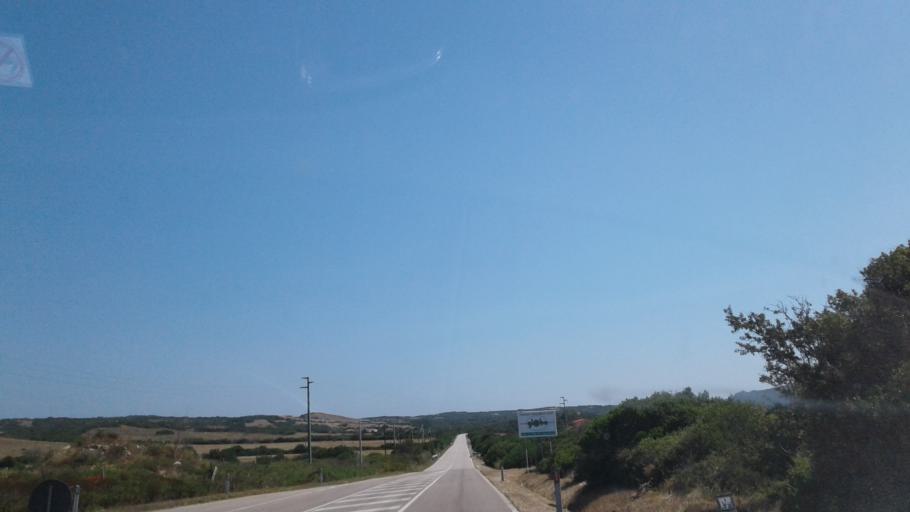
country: IT
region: Sardinia
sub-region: Provincia di Olbia-Tempio
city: Luogosanto
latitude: 41.1189
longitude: 9.2683
